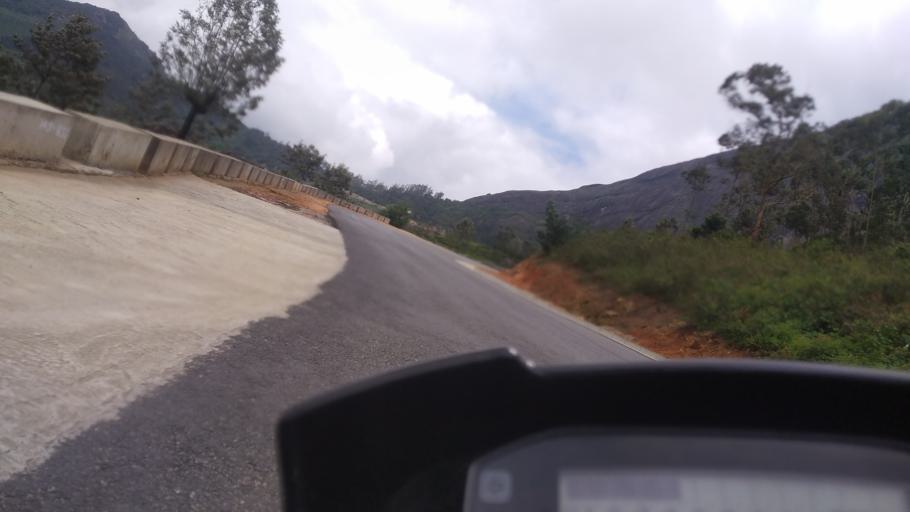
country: IN
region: Kerala
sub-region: Idukki
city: Munnar
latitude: 10.0423
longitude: 77.1112
